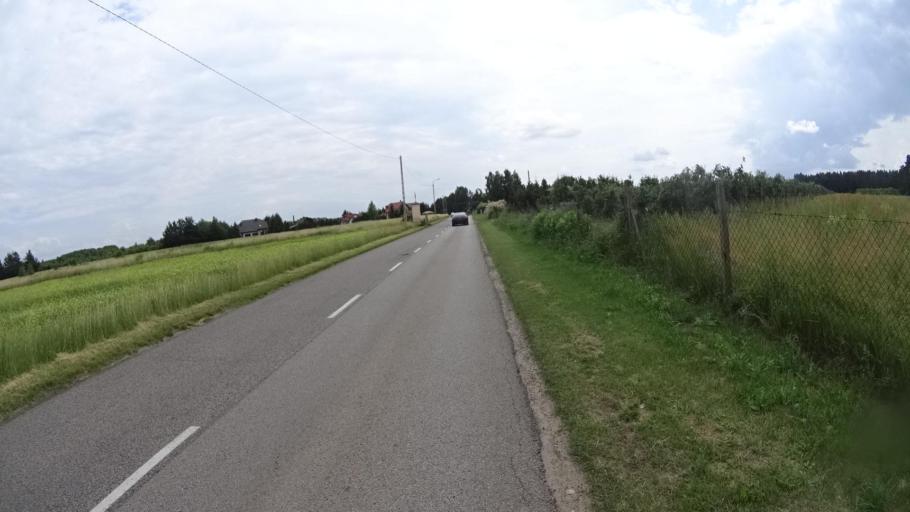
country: PL
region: Masovian Voivodeship
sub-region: Powiat piaseczynski
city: Tarczyn
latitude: 52.0037
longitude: 20.8124
